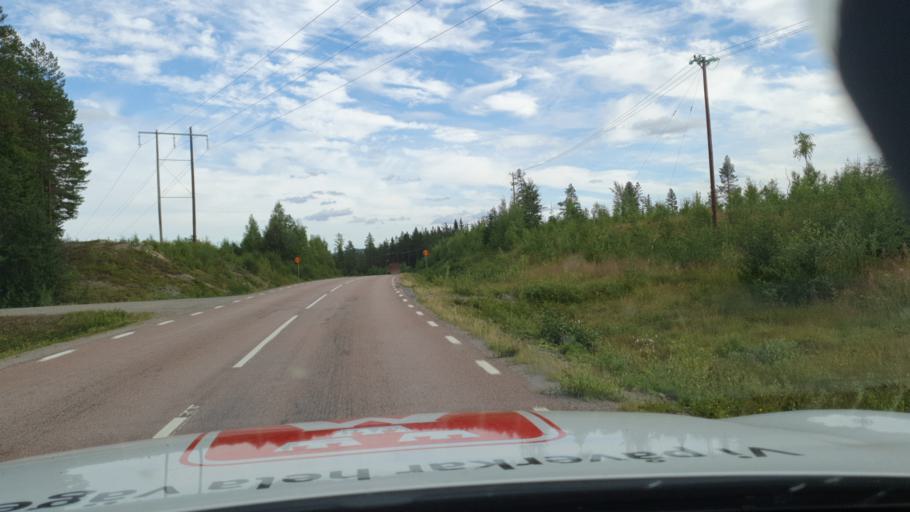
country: SE
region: Vaesternorrland
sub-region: Solleftea Kommun
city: As
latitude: 63.6071
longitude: 16.1220
